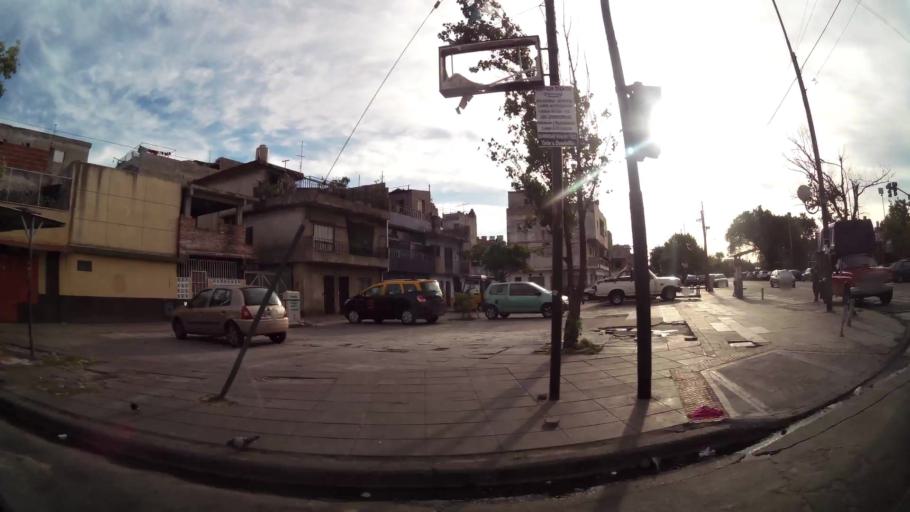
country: AR
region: Buenos Aires F.D.
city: Villa Lugano
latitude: -34.6437
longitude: -58.4415
